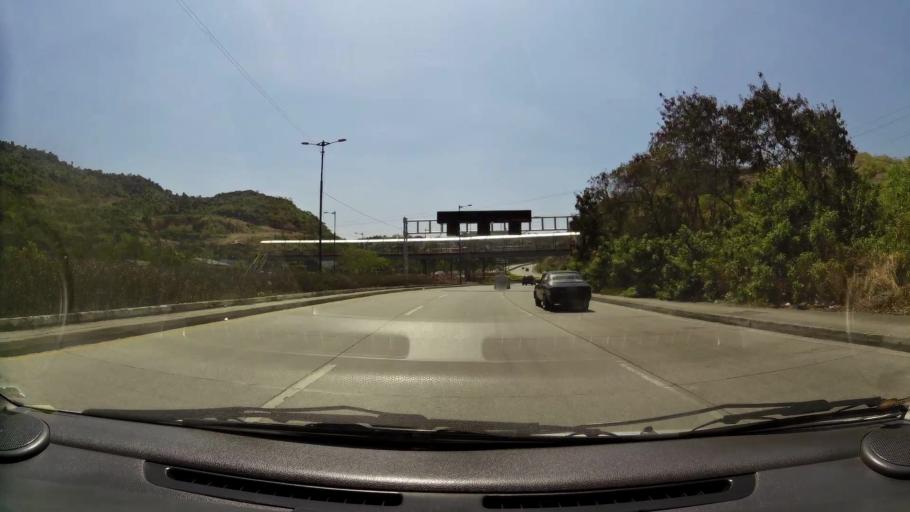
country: EC
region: Guayas
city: Guayaquil
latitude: -2.1862
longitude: -79.9325
